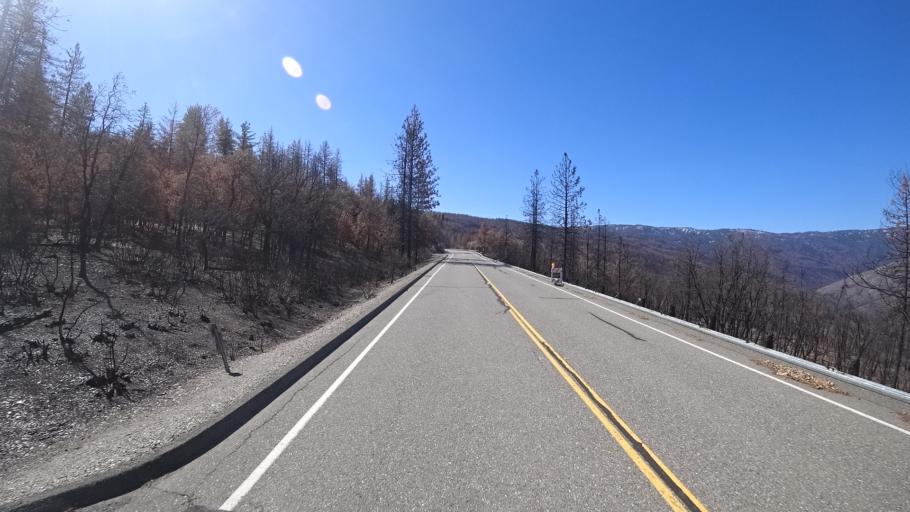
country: US
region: California
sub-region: Tehama County
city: Rancho Tehama Reserve
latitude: 39.6787
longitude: -122.7109
